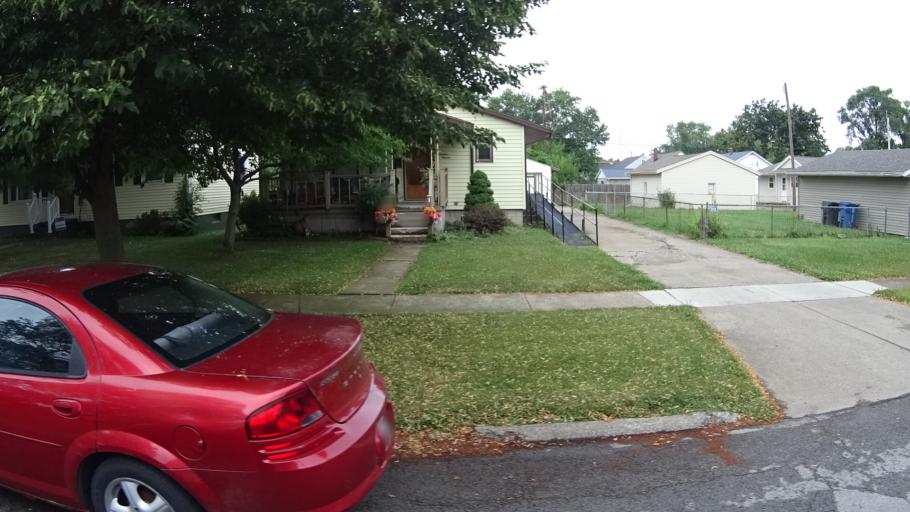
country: US
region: Ohio
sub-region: Erie County
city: Sandusky
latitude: 41.4450
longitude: -82.6871
